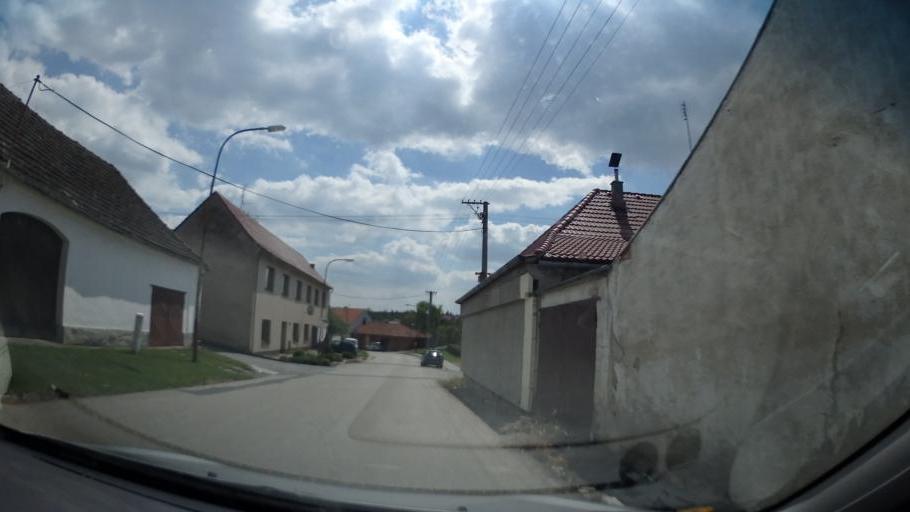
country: CZ
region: Vysocina
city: Mohelno
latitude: 49.1168
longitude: 16.1874
